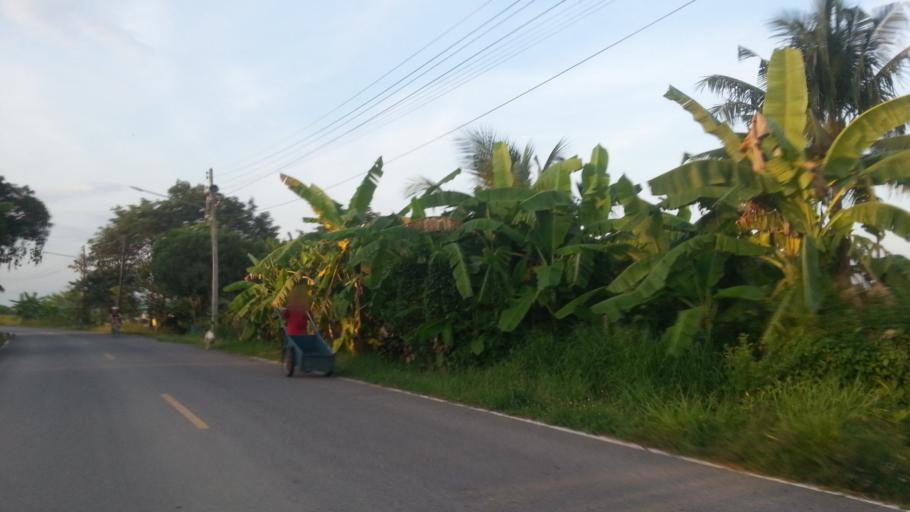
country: TH
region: Pathum Thani
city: Nong Suea
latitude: 14.0453
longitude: 100.8476
